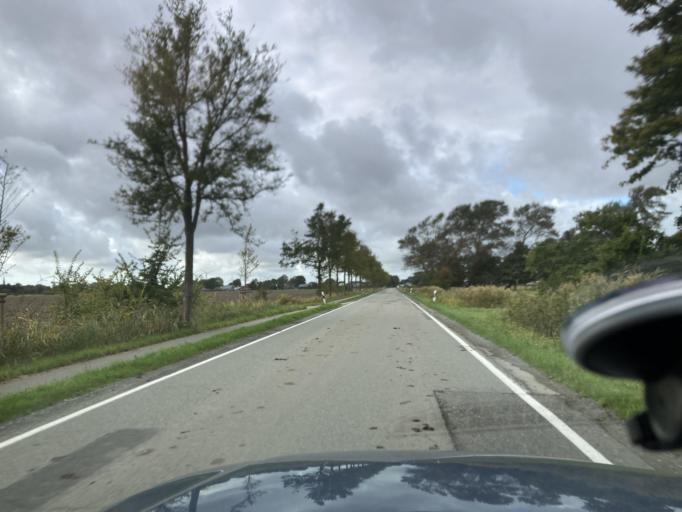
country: DE
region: Schleswig-Holstein
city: Neuenkirchen
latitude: 54.2338
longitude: 9.0089
